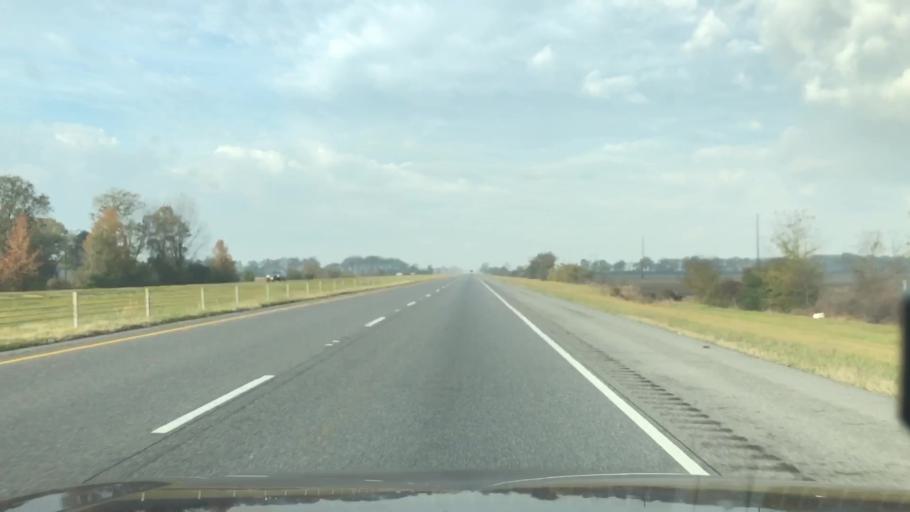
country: US
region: Louisiana
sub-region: Madison Parish
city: Tallulah
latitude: 32.4212
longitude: -91.3227
